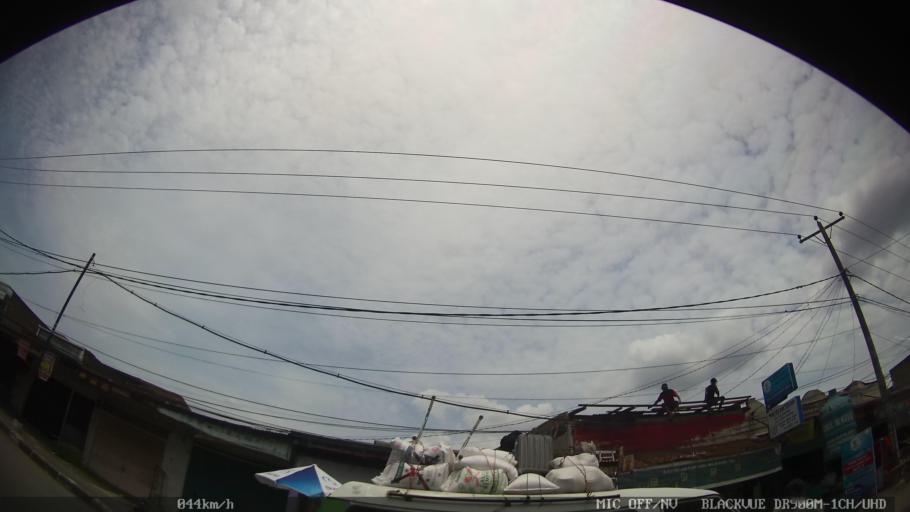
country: ID
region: North Sumatra
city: Deli Tua
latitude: 3.5368
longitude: 98.6507
